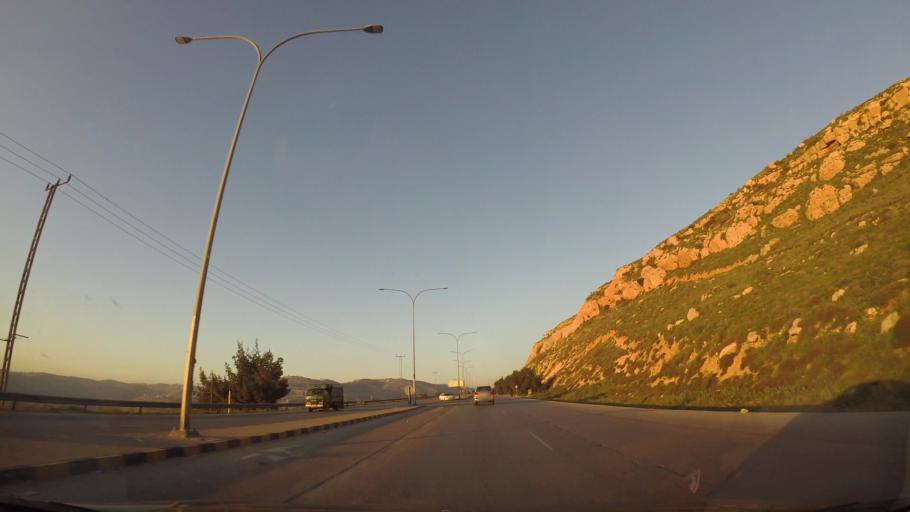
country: JO
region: Amman
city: Umm as Summaq
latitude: 31.8704
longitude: 35.7697
